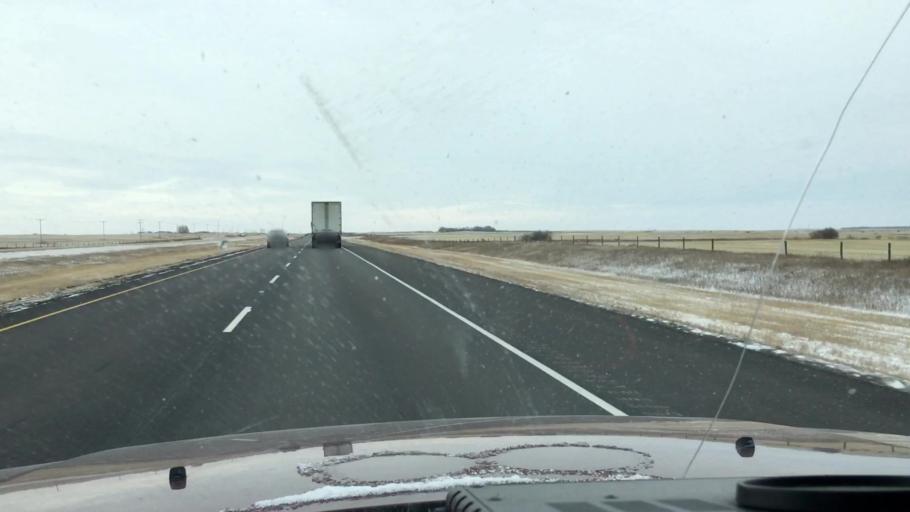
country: CA
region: Saskatchewan
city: Saskatoon
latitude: 51.7984
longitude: -106.4885
